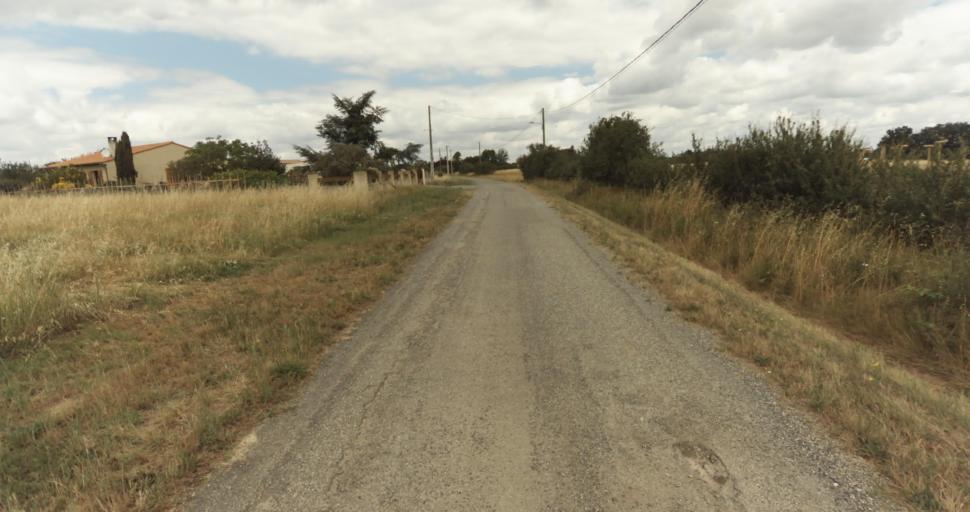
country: FR
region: Midi-Pyrenees
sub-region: Departement de la Haute-Garonne
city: Fontenilles
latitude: 43.5459
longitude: 1.1951
